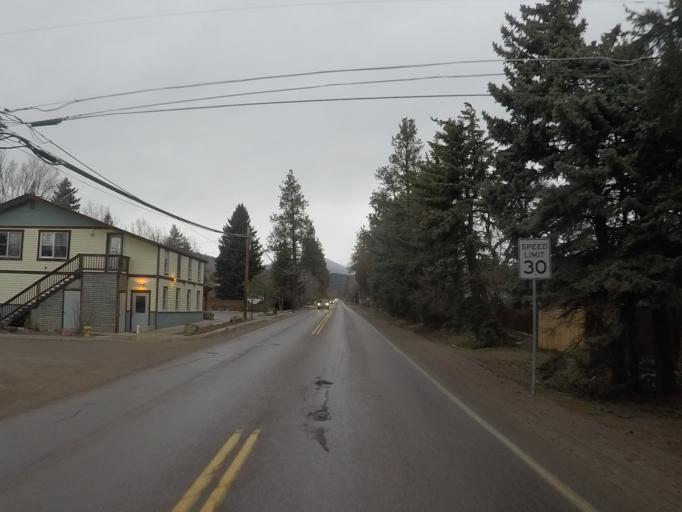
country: US
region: Montana
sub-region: Missoula County
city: East Missoula
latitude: 46.8869
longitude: -113.9657
